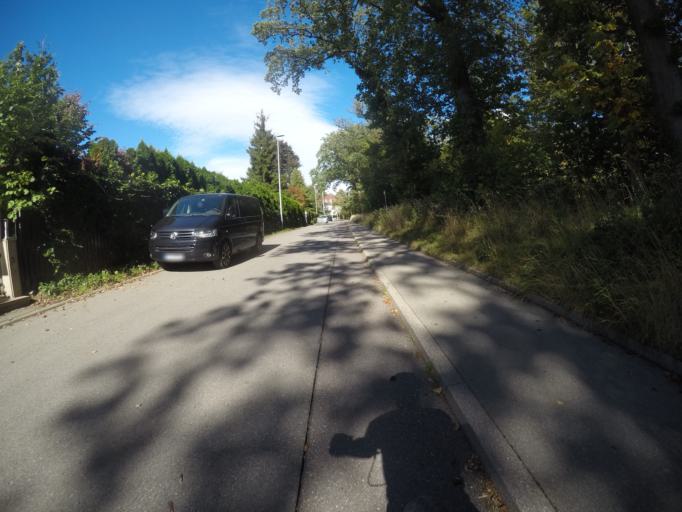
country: DE
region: Baden-Wuerttemberg
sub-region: Regierungsbezirk Stuttgart
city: Stuttgart
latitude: 48.7482
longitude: 9.1814
